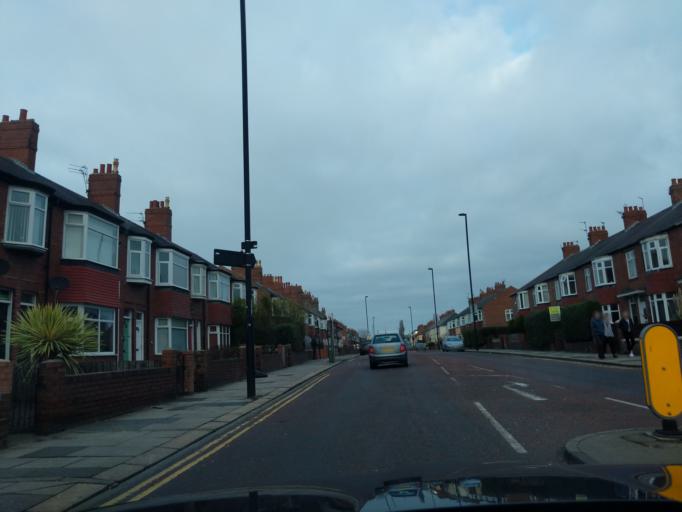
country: GB
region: England
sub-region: Gateshead
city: Gateshead
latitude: 54.9893
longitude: -1.5780
